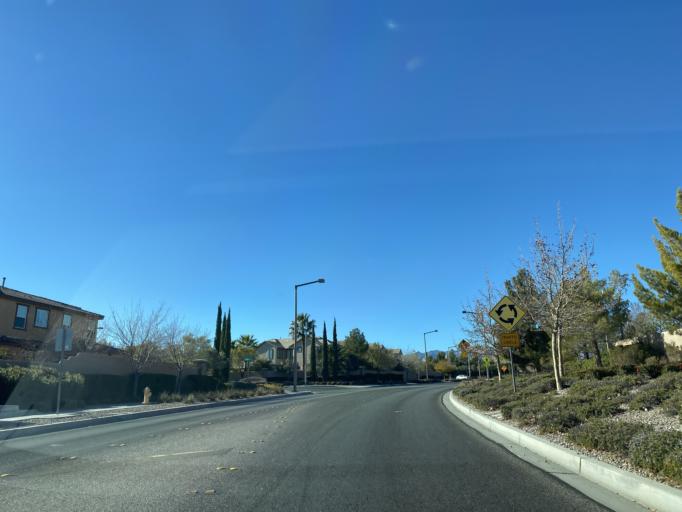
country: US
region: Nevada
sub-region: Clark County
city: Summerlin South
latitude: 36.1619
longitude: -115.3428
